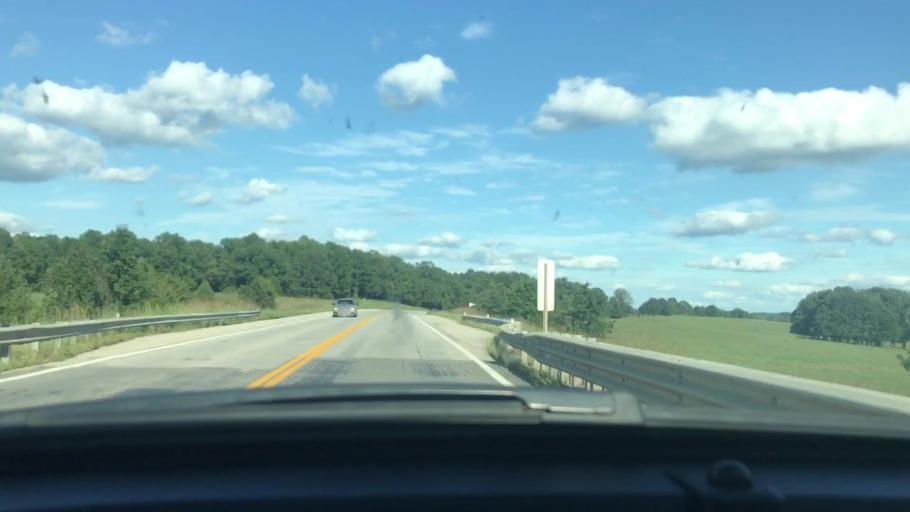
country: US
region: Missouri
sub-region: Howell County
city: West Plains
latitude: 36.6609
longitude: -91.7139
